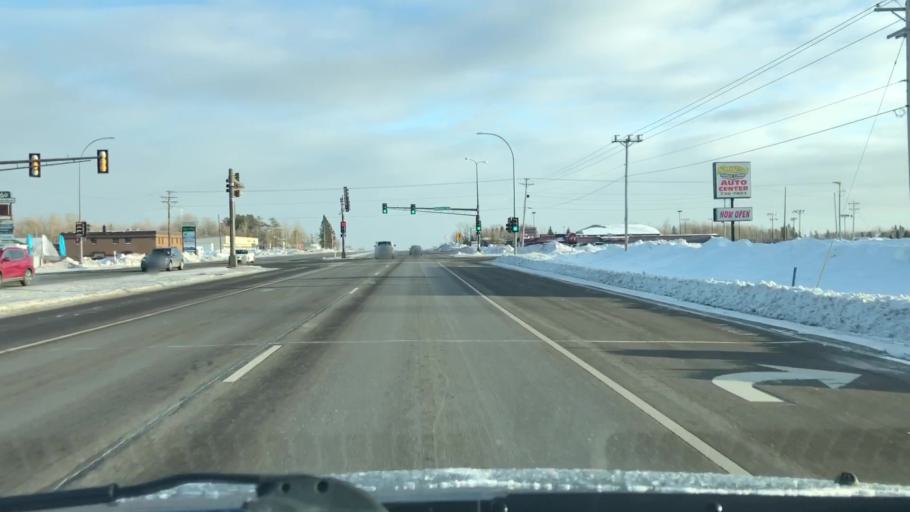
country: US
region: Minnesota
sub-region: Saint Louis County
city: Hermantown
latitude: 46.8278
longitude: -92.1960
